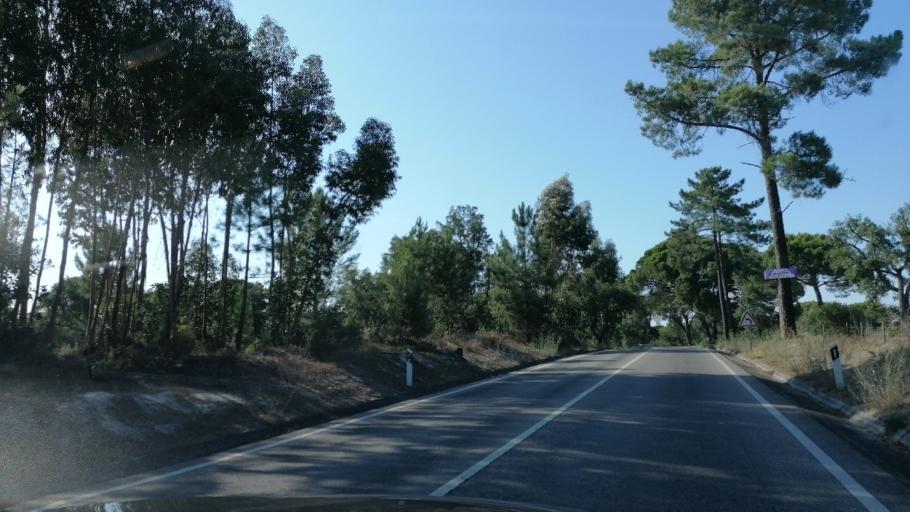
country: PT
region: Santarem
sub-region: Coruche
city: Coruche
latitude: 38.9750
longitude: -8.5397
